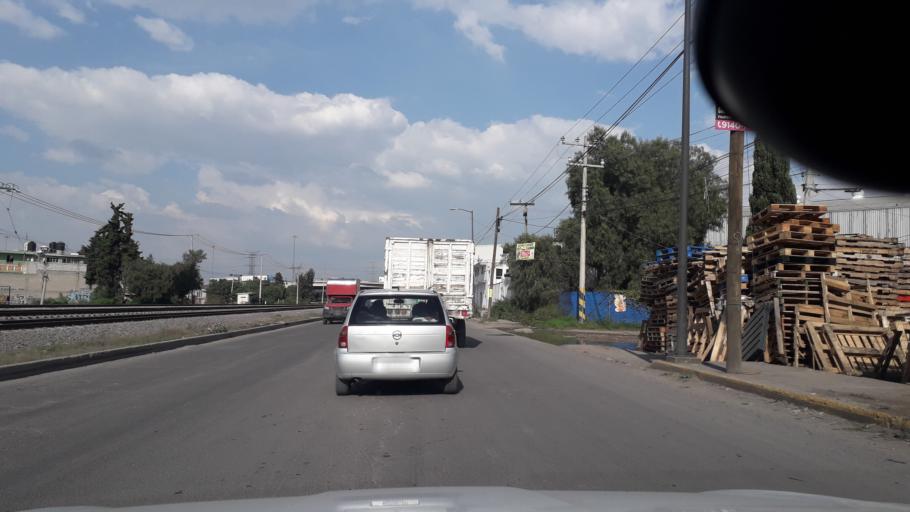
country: MX
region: Mexico
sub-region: Tultitlan
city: Colonia Lazaro Cardenas (Los Hornos)
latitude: 19.6342
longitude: -99.1600
